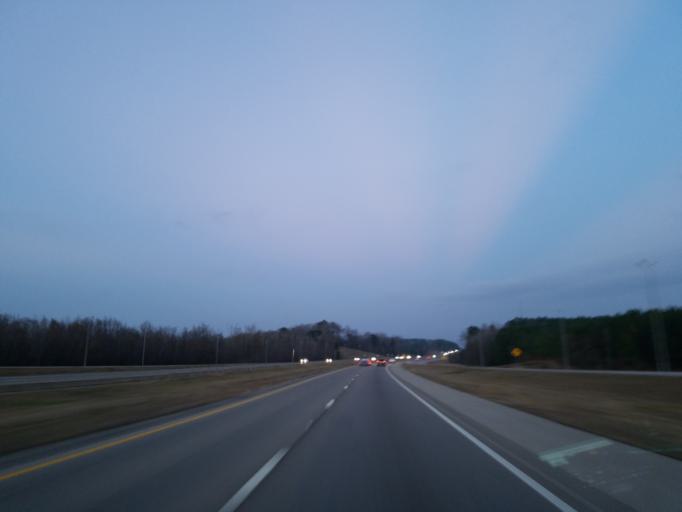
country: US
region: Alabama
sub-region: Sumter County
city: York
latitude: 32.4387
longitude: -88.4342
